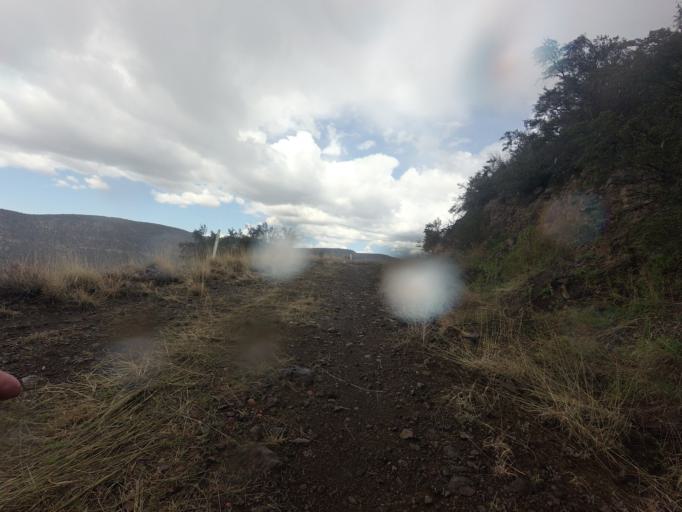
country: US
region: Arizona
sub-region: Gila County
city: Pine
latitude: 34.4046
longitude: -111.5937
